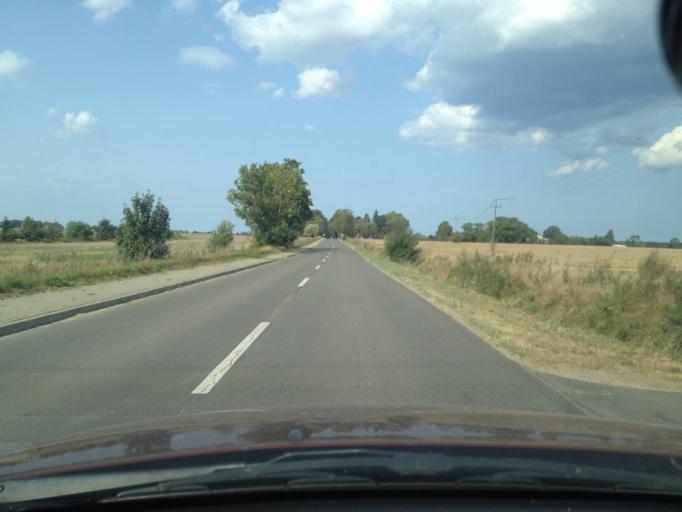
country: PL
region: West Pomeranian Voivodeship
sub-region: Powiat gryficki
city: Pobierowo
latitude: 54.0146
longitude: 14.8694
